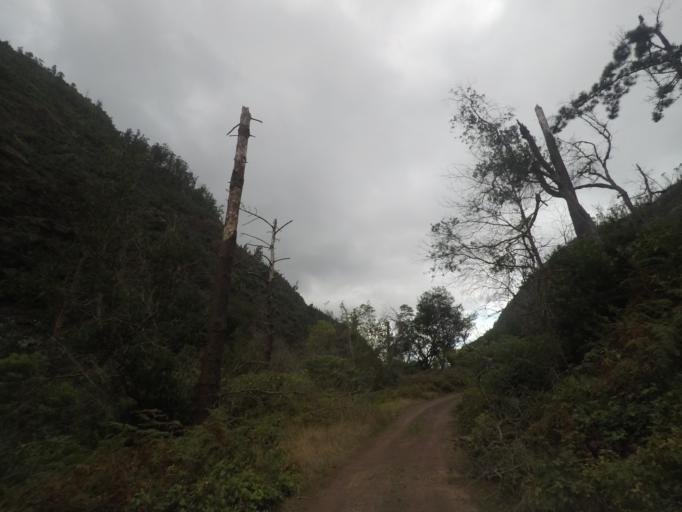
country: PT
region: Madeira
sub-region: Funchal
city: Nossa Senhora do Monte
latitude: 32.6933
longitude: -16.9172
